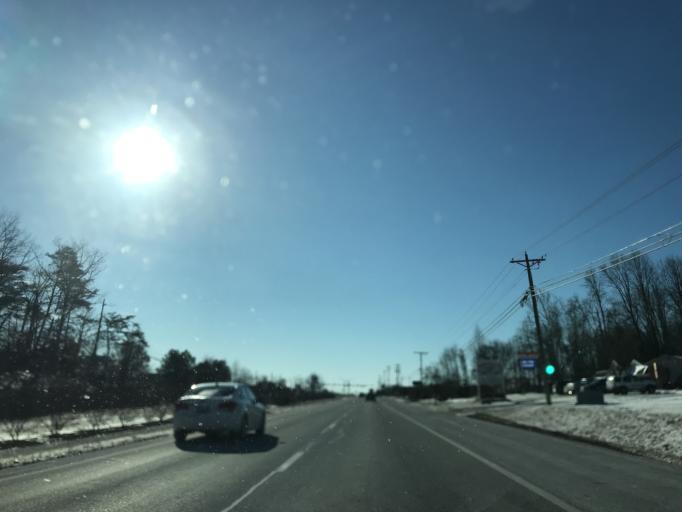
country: US
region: Maryland
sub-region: Charles County
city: La Plata
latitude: 38.5517
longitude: -76.9859
